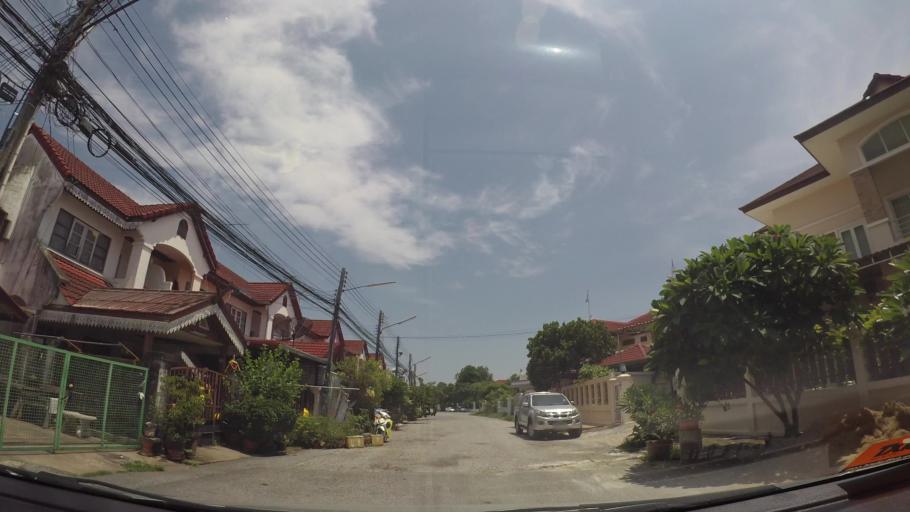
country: TH
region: Chon Buri
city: Chon Buri
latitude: 13.3317
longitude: 100.9395
